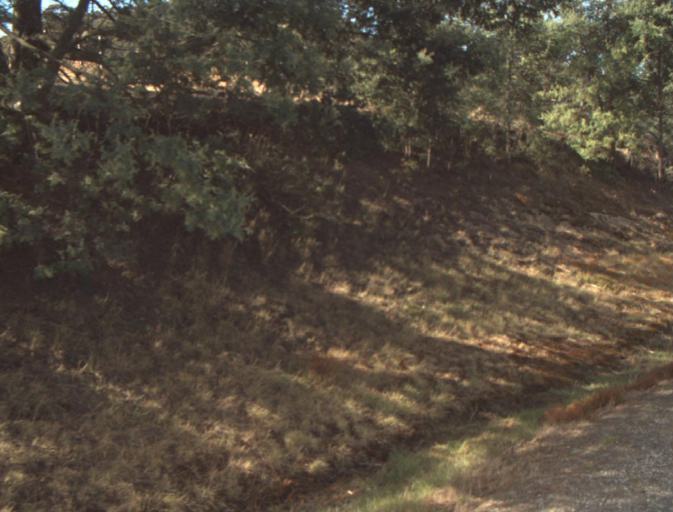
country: AU
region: Tasmania
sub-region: Launceston
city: Mayfield
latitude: -41.2915
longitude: 147.2165
